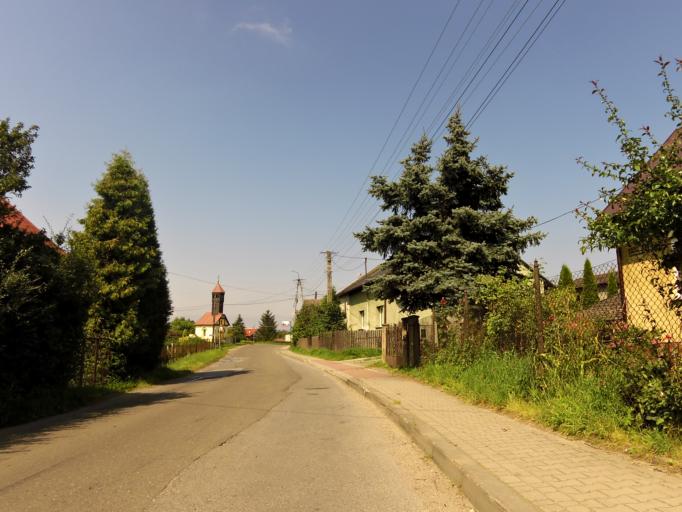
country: PL
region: Silesian Voivodeship
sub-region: Powiat zywiecki
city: Wieprz
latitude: 49.6375
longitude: 19.1740
